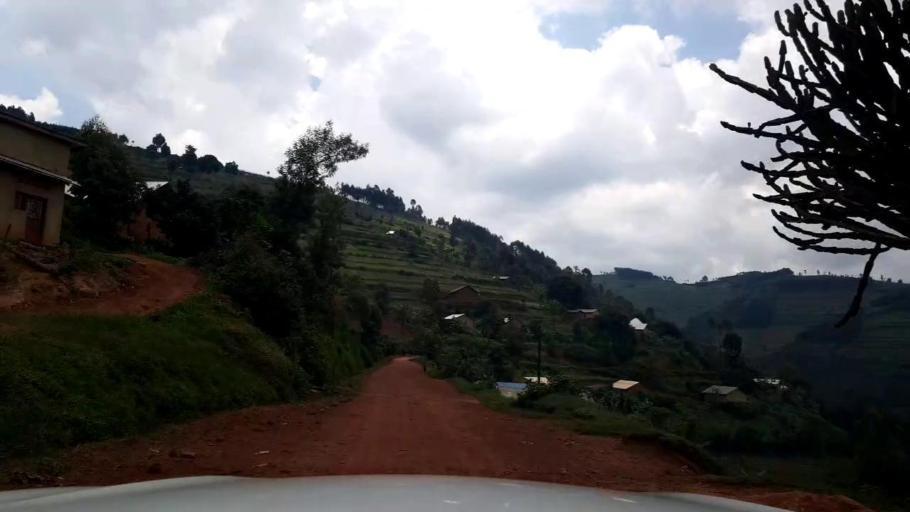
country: RW
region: Northern Province
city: Byumba
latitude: -1.4787
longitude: 29.9003
